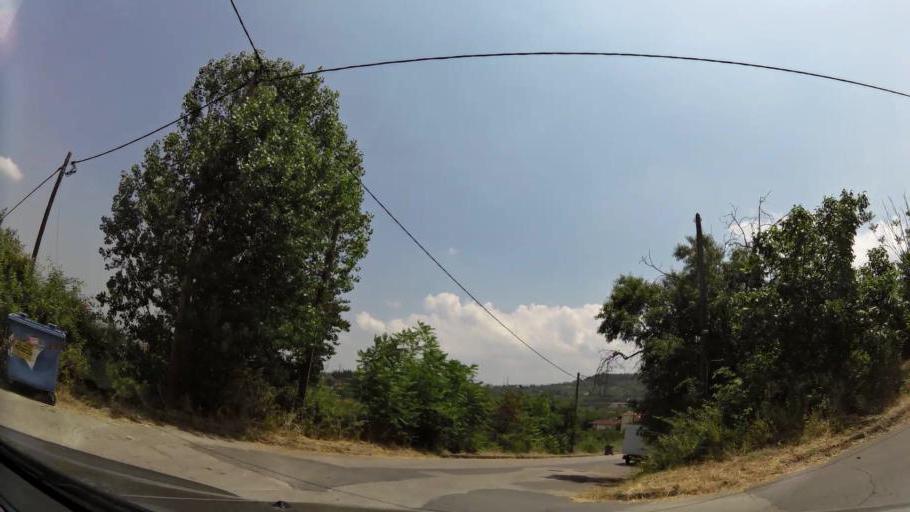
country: GR
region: Central Macedonia
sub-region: Nomos Imathias
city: Veroia
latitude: 40.5157
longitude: 22.1870
